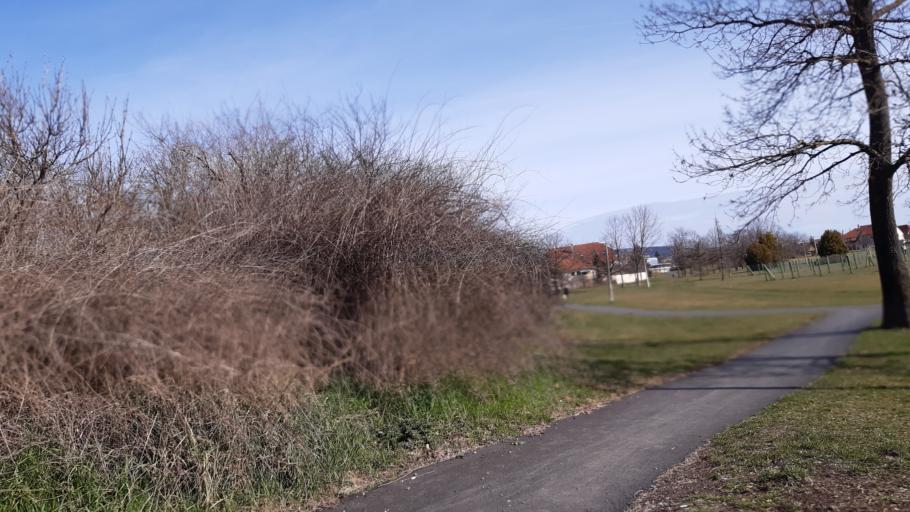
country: HU
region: Baranya
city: Pellerd
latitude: 46.0605
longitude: 18.1812
